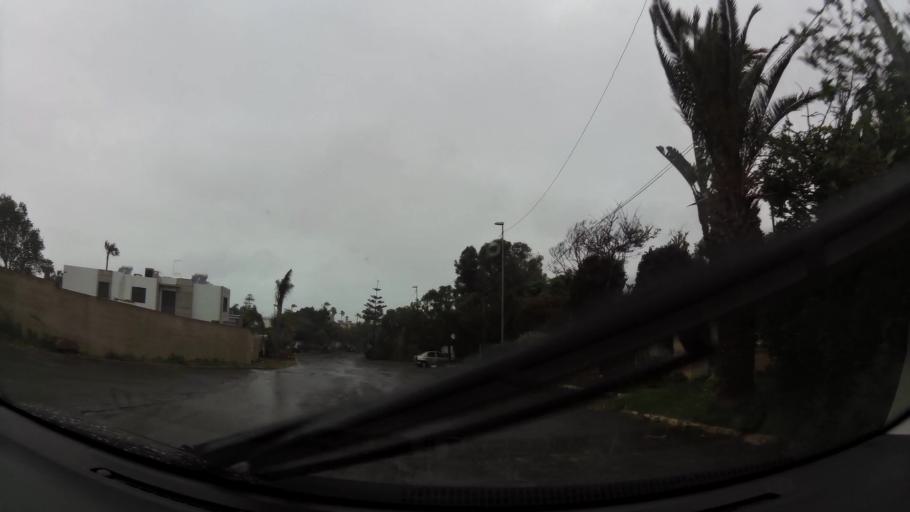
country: MA
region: Grand Casablanca
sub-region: Casablanca
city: Casablanca
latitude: 33.5857
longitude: -7.6739
